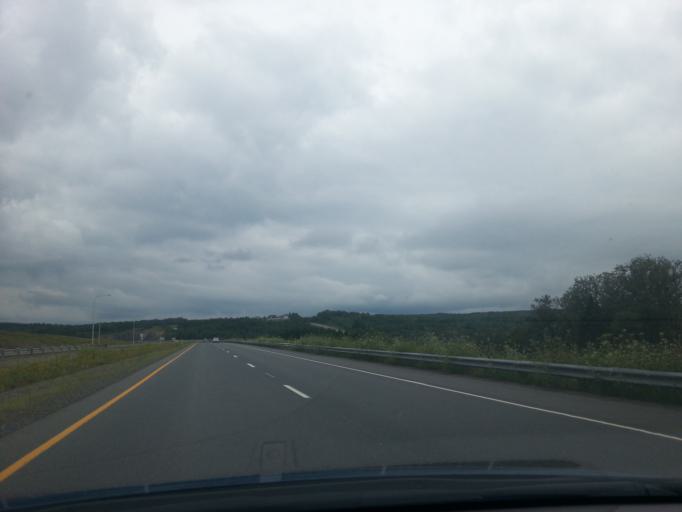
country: US
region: Maine
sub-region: Aroostook County
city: Limestone
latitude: 47.0146
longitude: -67.7561
